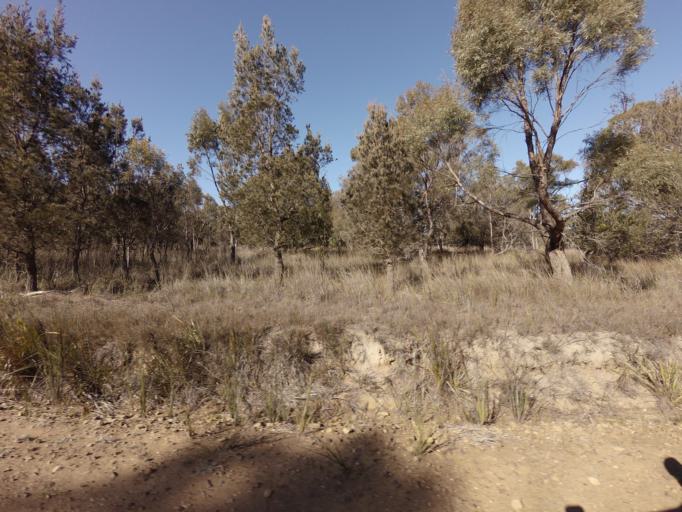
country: AU
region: Tasmania
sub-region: Sorell
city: Sorell
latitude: -42.3489
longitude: 147.9729
